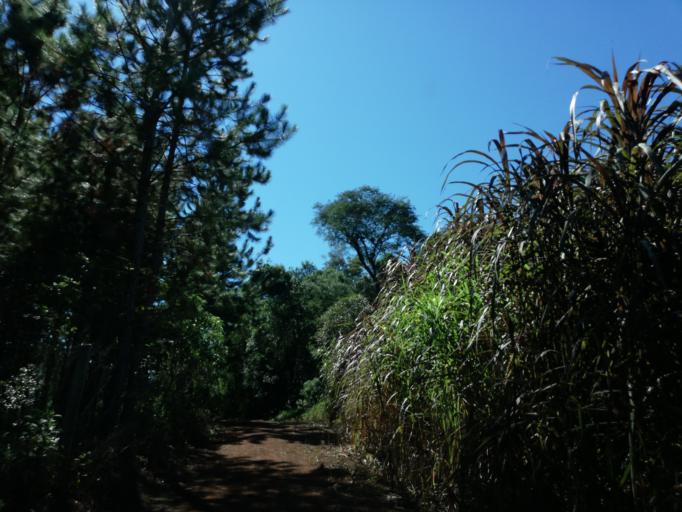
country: AR
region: Misiones
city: El Soberbio
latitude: -27.0639
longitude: -54.3781
